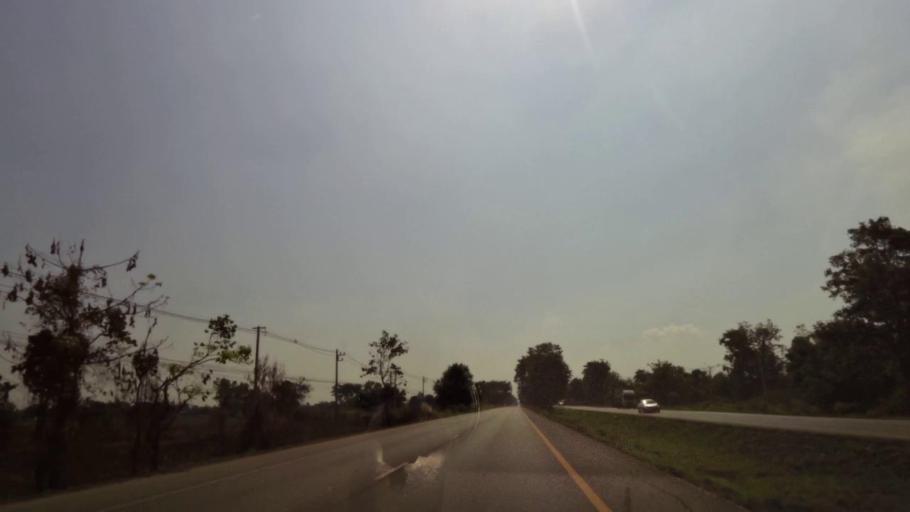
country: TH
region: Phichit
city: Bueng Na Rang
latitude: 16.2917
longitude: 100.1280
